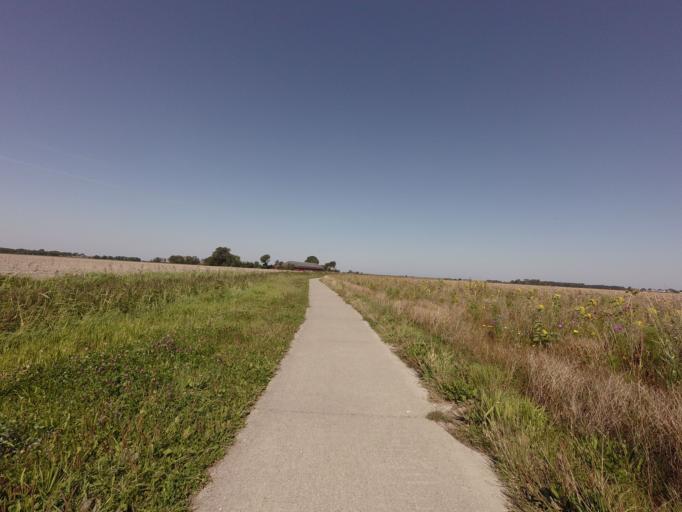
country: NL
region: Friesland
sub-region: Gemeente Dongeradeel
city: Anjum
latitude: 53.3891
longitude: 6.0662
